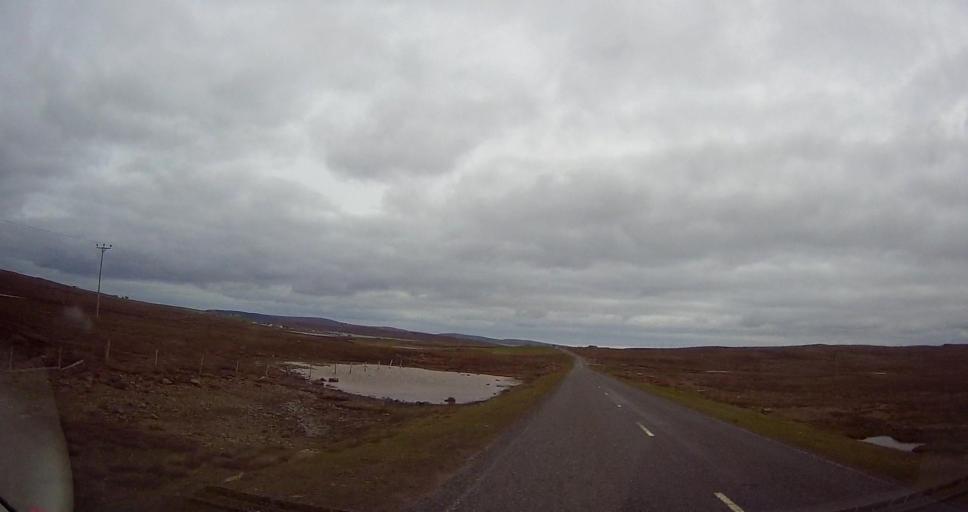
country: GB
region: Scotland
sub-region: Shetland Islands
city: Shetland
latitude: 60.7084
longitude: -0.9191
